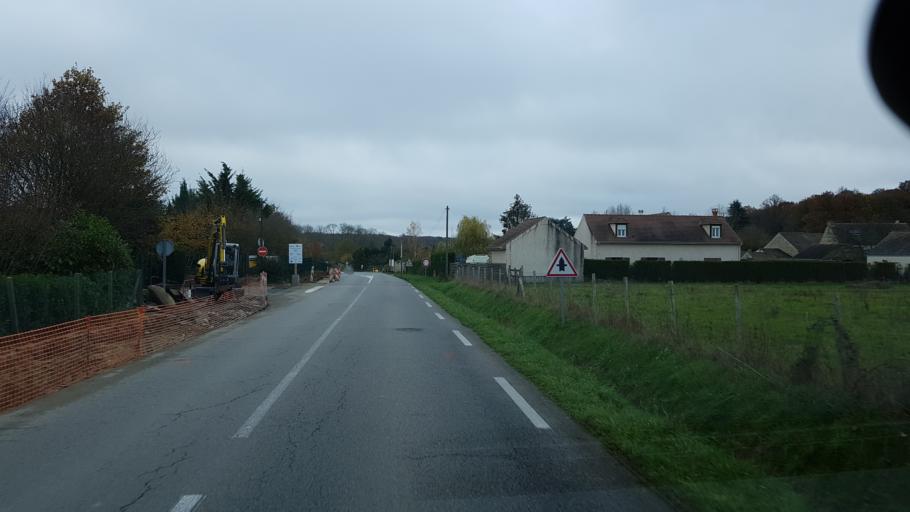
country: FR
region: Ile-de-France
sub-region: Departement des Yvelines
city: Chevreuse
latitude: 48.7186
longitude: 2.0106
